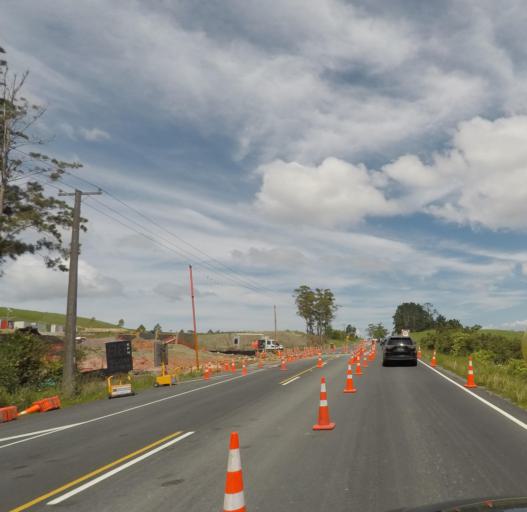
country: NZ
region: Auckland
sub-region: Auckland
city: Rothesay Bay
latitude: -36.6697
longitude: 174.6819
